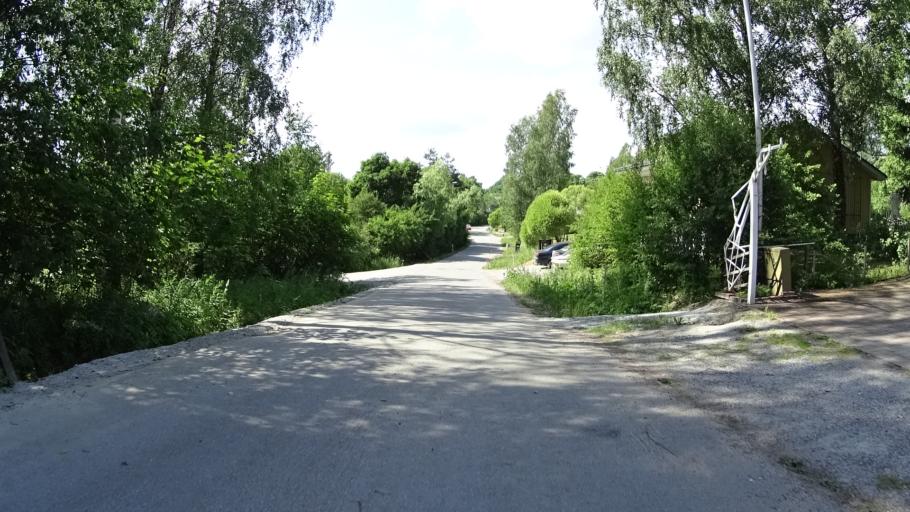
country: FI
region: Uusimaa
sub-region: Raaseporin
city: Karis
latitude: 60.0856
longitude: 23.6509
